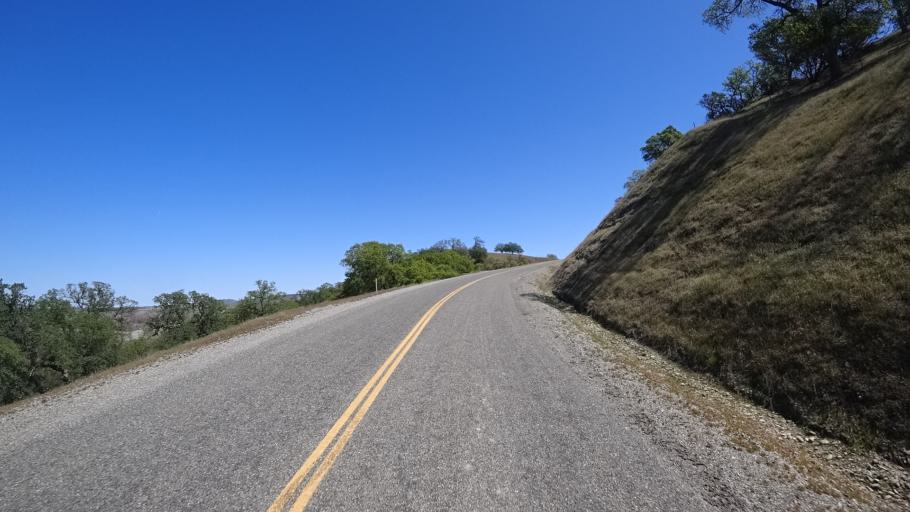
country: US
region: California
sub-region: Glenn County
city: Orland
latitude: 39.7419
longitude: -122.3846
